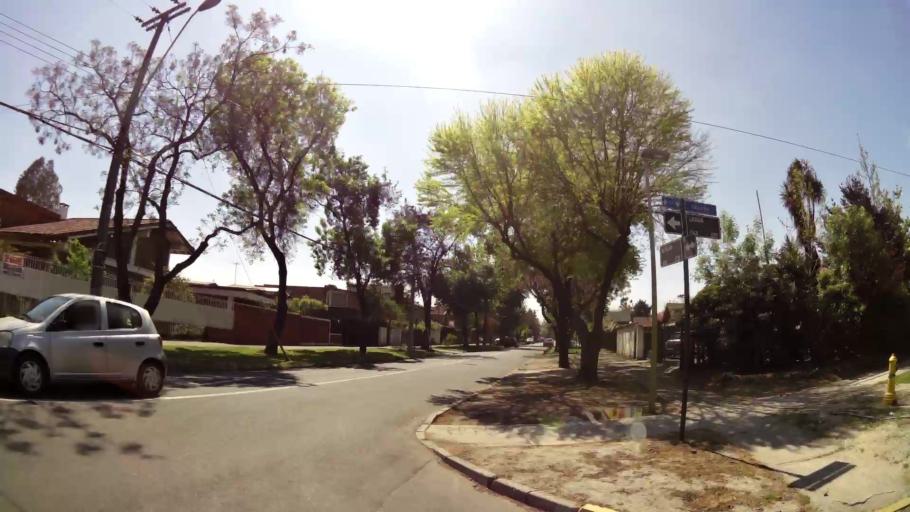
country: CL
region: Santiago Metropolitan
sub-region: Provincia de Santiago
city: Villa Presidente Frei, Nunoa, Santiago, Chile
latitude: -33.4269
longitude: -70.5604
